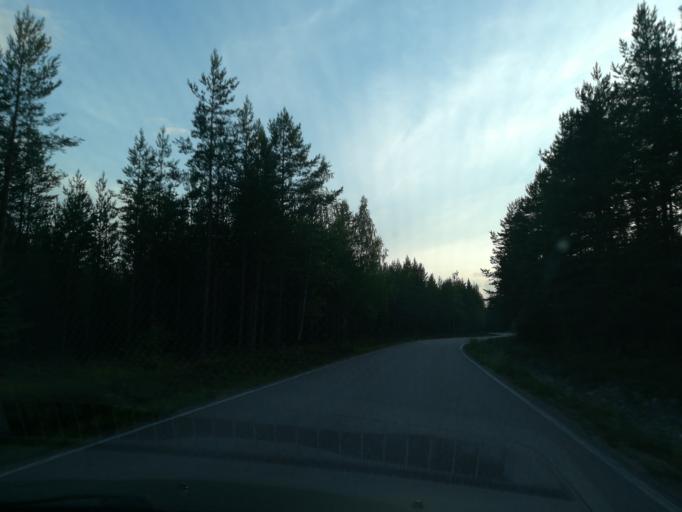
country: FI
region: South Karelia
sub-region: Lappeenranta
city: Joutseno
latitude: 61.3460
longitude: 28.4264
